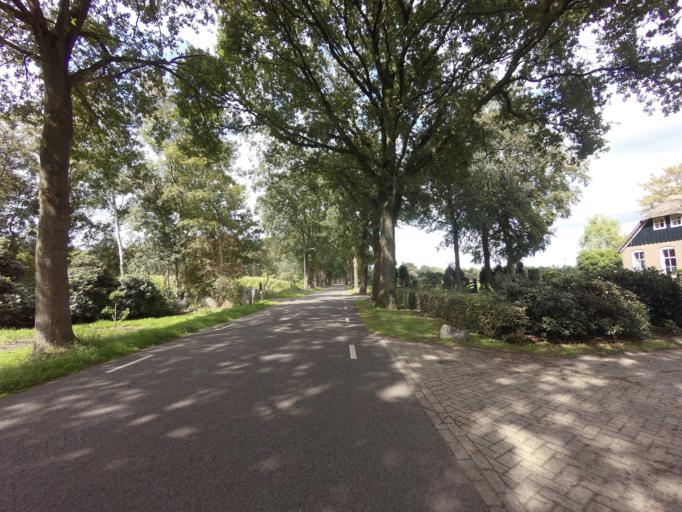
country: NL
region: Drenthe
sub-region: Gemeente De Wolden
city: Ruinen
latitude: 52.7131
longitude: 6.3367
